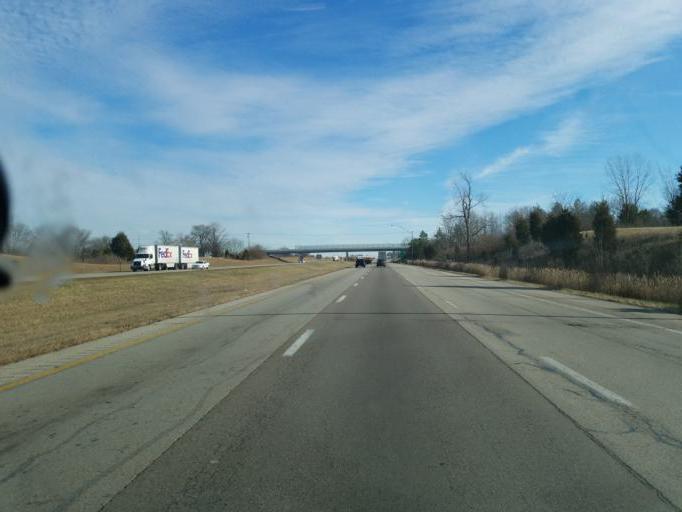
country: US
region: Ohio
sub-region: Preble County
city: New Paris
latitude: 39.8285
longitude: -84.7969
